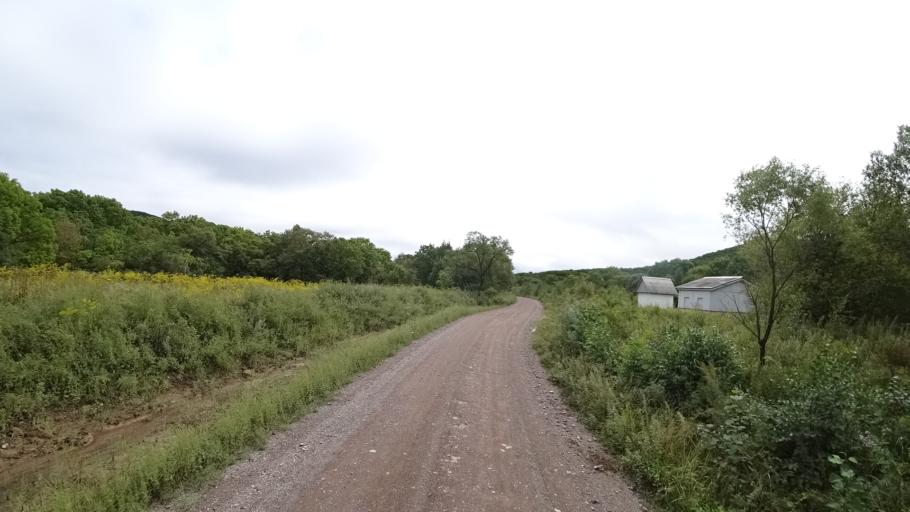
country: RU
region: Primorskiy
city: Monastyrishche
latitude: 44.1656
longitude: 132.5351
